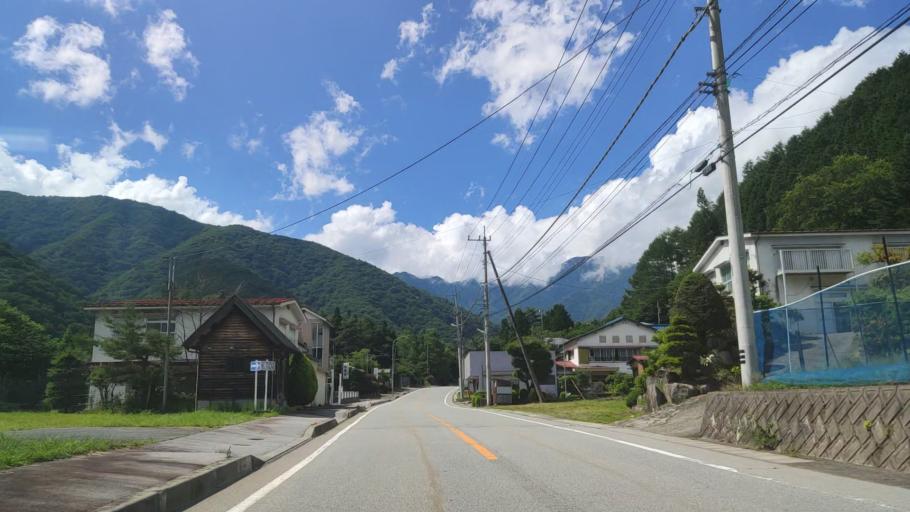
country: JP
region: Yamanashi
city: Enzan
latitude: 35.8479
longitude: 138.7611
